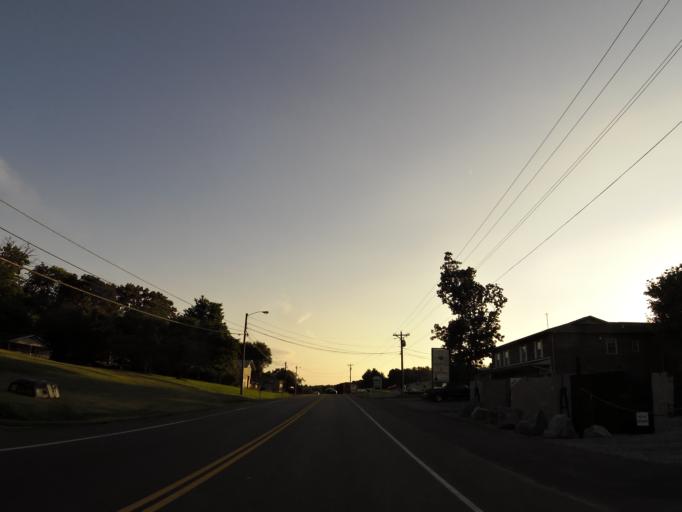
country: US
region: Tennessee
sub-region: Jefferson County
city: Dandridge
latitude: 36.0313
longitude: -83.3907
